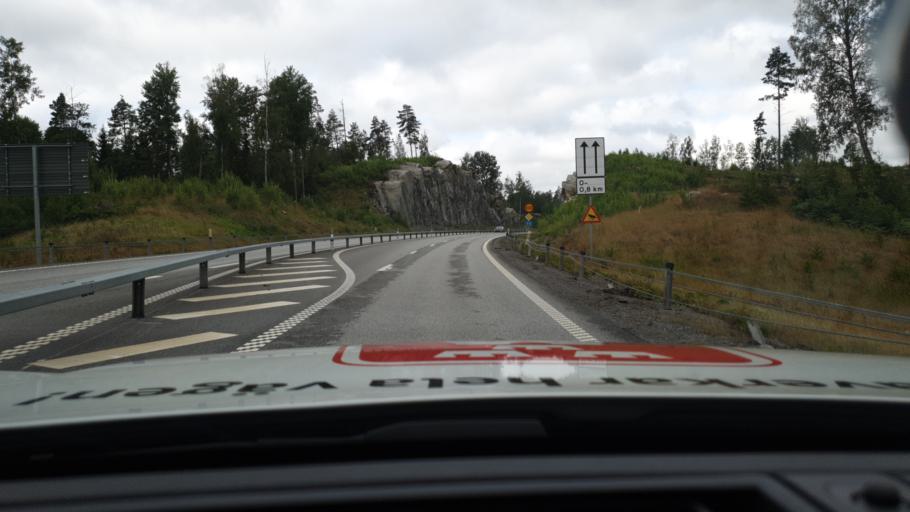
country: SE
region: Soedermanland
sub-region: Flens Kommun
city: Malmkoping
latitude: 59.1307
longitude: 16.6865
